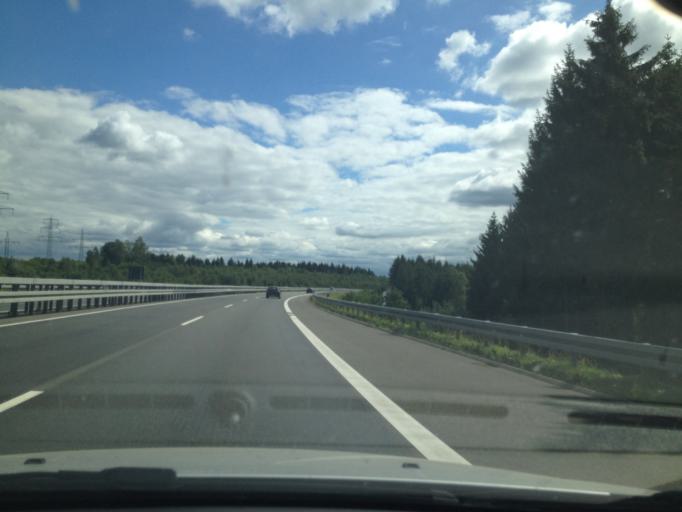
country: DE
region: North Rhine-Westphalia
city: Kreuztal
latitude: 50.9835
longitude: 7.9388
